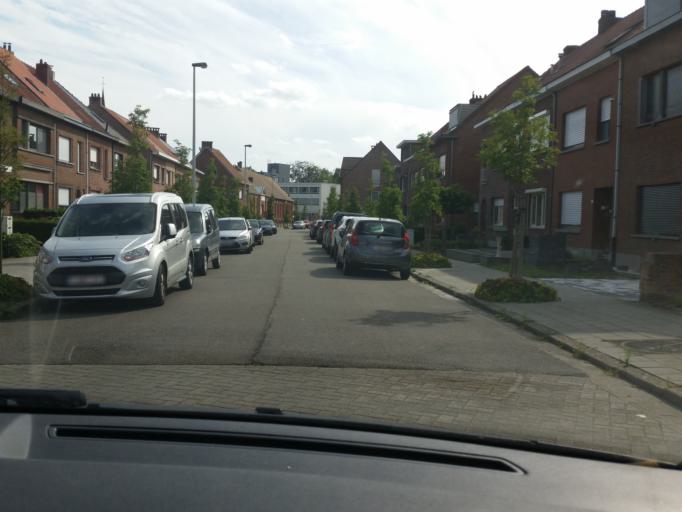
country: BE
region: Flanders
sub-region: Provincie Antwerpen
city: Rumst
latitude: 51.0804
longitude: 4.4279
